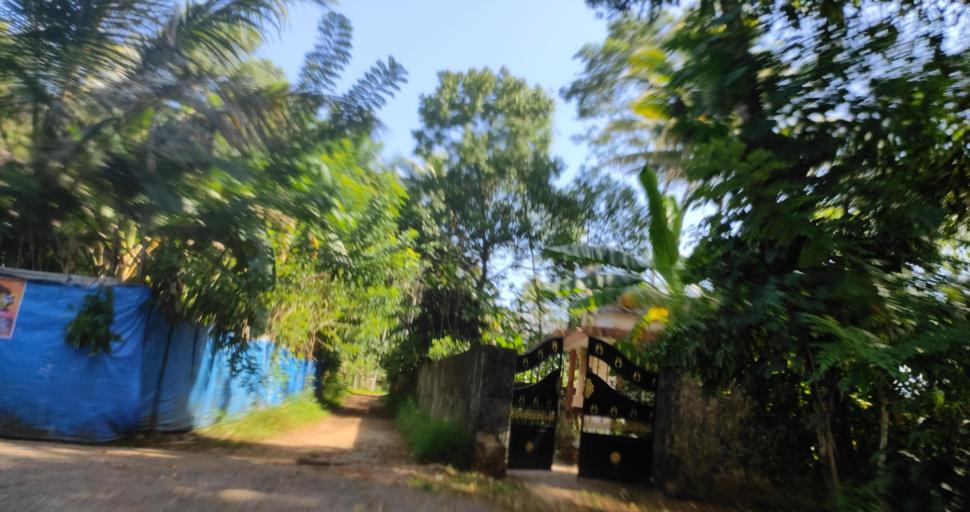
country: IN
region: Kerala
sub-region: Alappuzha
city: Shertallai
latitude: 9.6330
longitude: 76.3406
